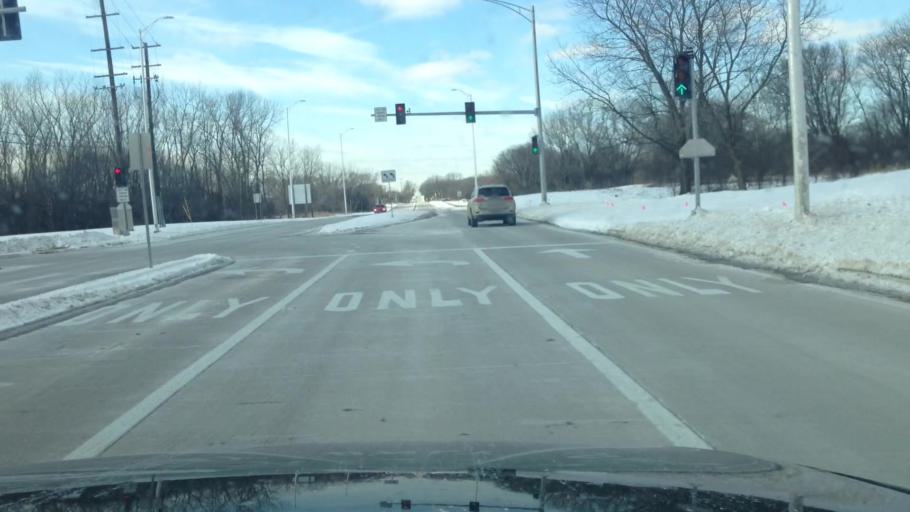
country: US
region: Illinois
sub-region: Cook County
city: Hoffman Estates
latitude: 42.0671
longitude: -88.0859
